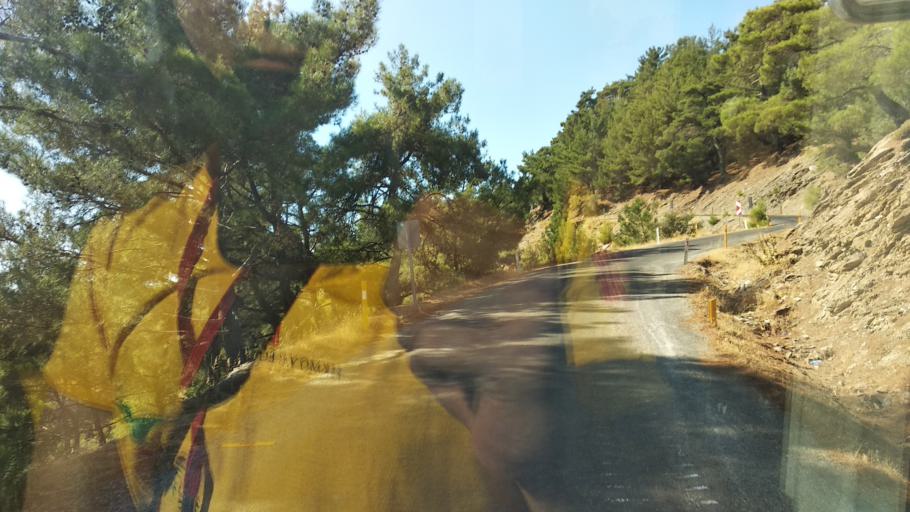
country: TR
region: Izmir
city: Gaziemir
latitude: 38.2960
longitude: 26.9997
